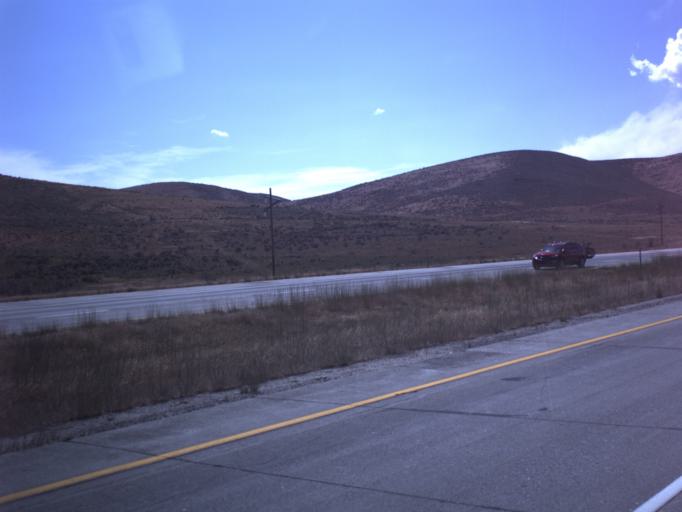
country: US
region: Utah
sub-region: Box Elder County
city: Garland
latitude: 41.8068
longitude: -112.3325
